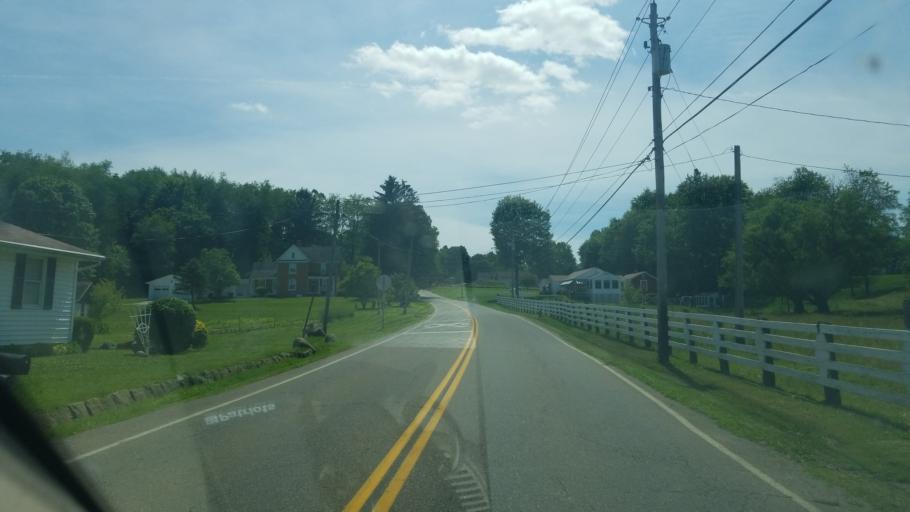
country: US
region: Ohio
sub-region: Stark County
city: Massillon
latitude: 40.8108
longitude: -81.5388
